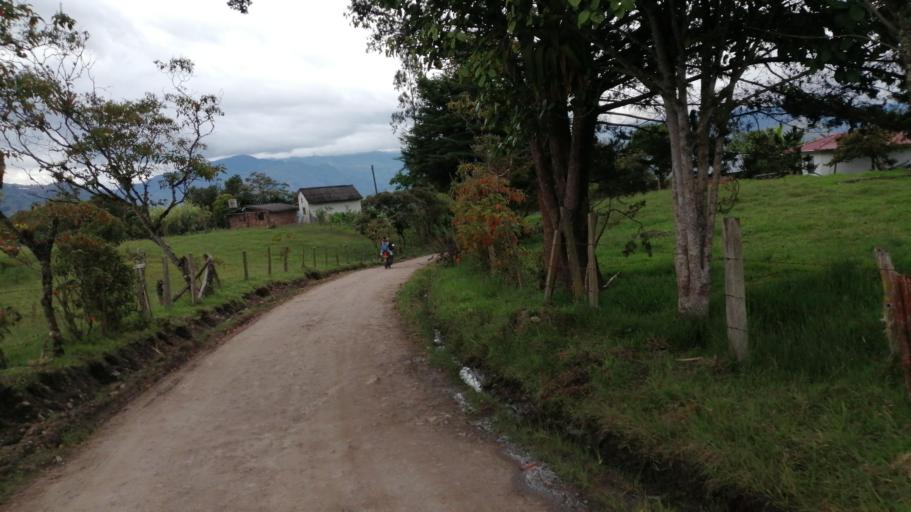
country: CO
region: Boyaca
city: Chinavita
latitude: 5.1345
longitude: -73.3948
